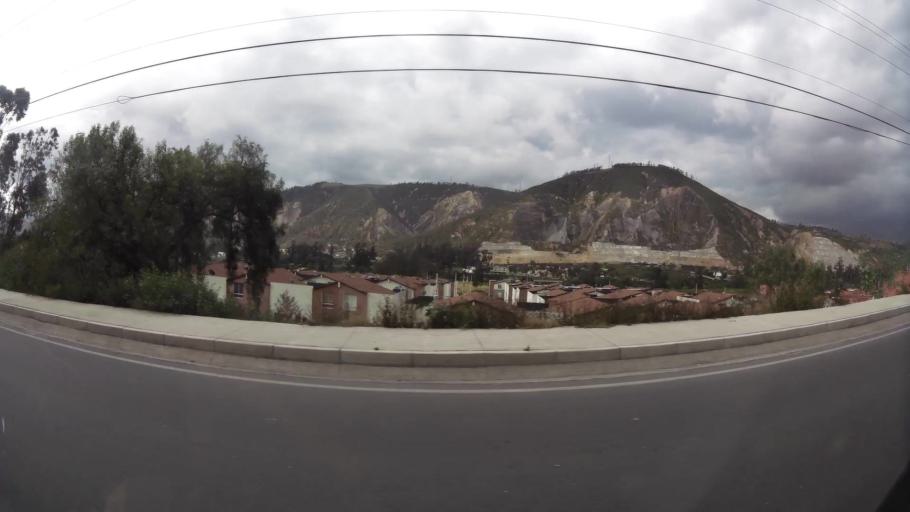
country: EC
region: Pichincha
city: Quito
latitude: -0.0466
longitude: -78.4549
